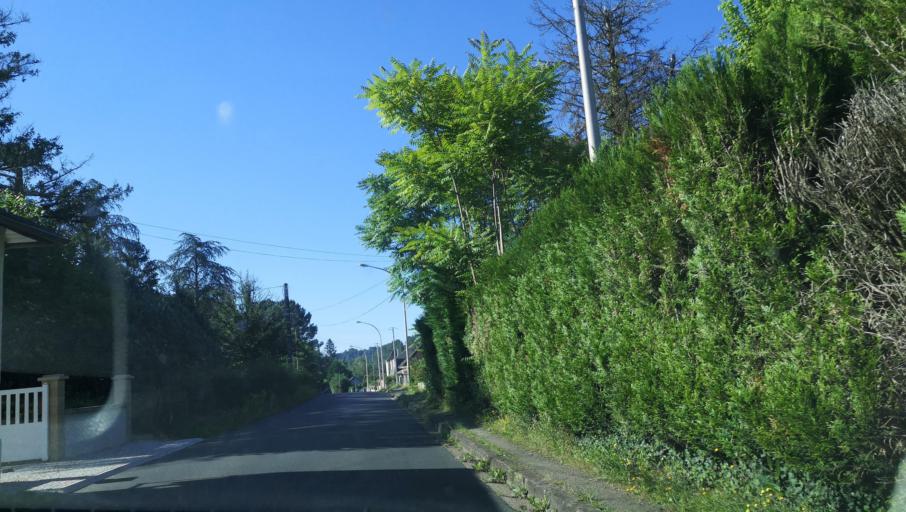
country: FR
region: Limousin
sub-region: Departement de la Correze
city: Brive-la-Gaillarde
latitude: 45.1459
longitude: 1.5488
